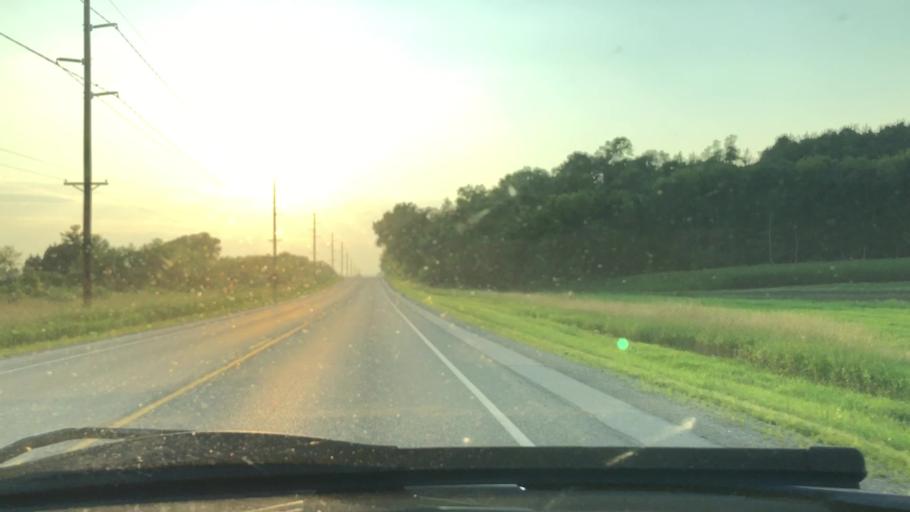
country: US
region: Wisconsin
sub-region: Dane County
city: Black Earth
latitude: 43.1292
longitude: -89.7166
